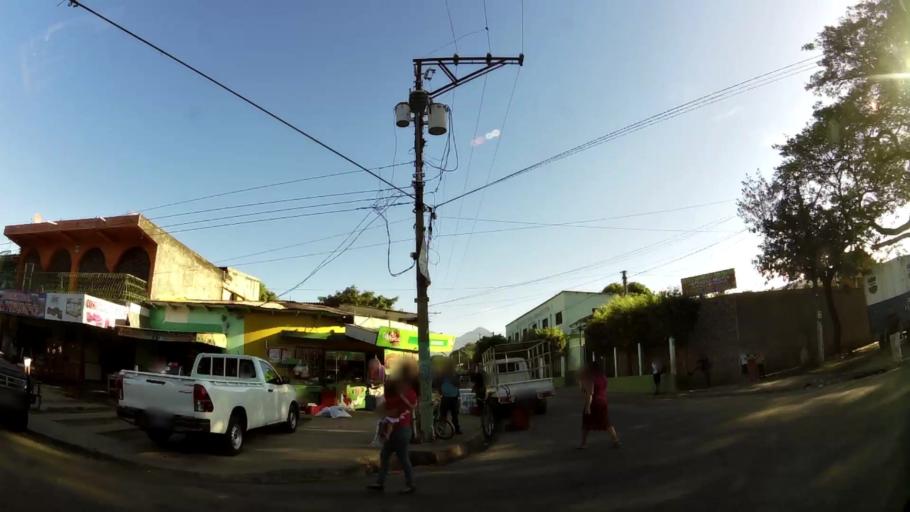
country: SV
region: Sonsonate
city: Sonsonate
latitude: 13.7163
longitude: -89.7215
